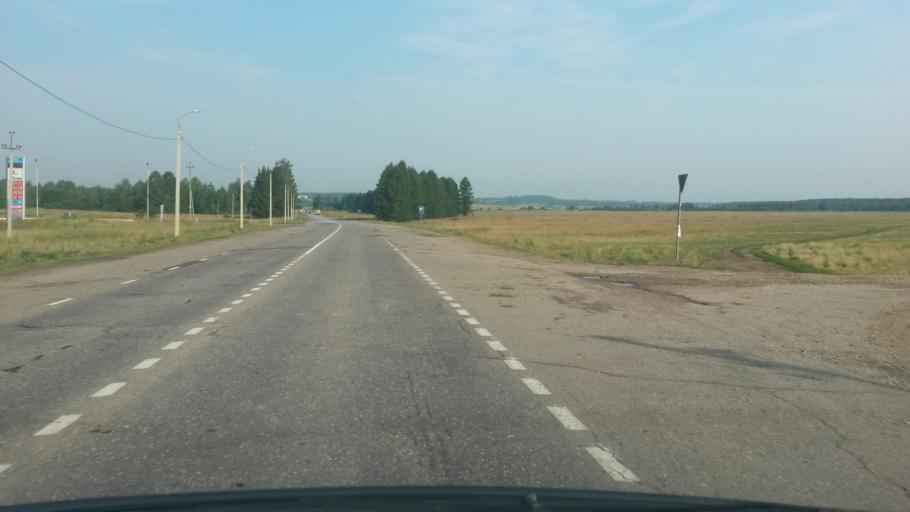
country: RU
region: Jaroslavl
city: Gavrilov-Yam
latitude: 57.3353
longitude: 39.8096
